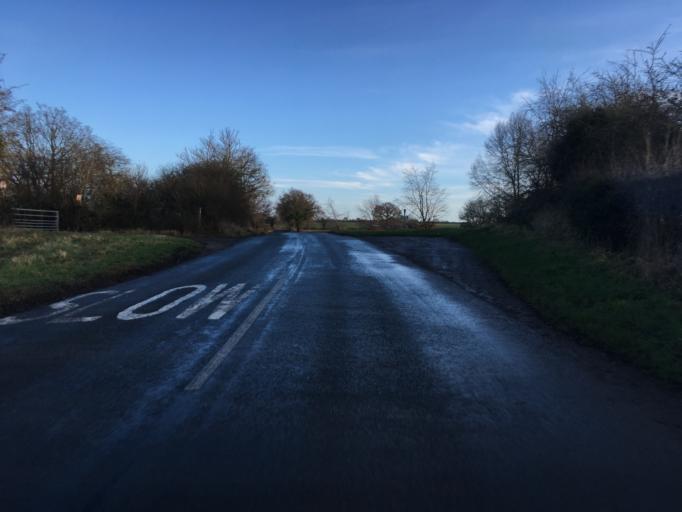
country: GB
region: England
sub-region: Warwickshire
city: Henley in Arden
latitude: 52.2472
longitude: -1.7922
